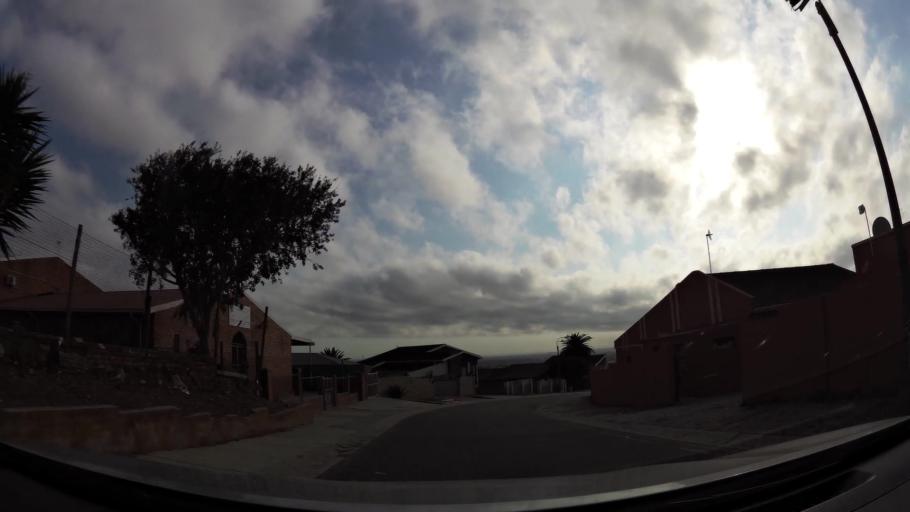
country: ZA
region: Eastern Cape
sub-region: Nelson Mandela Bay Metropolitan Municipality
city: Port Elizabeth
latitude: -33.9244
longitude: 25.5523
